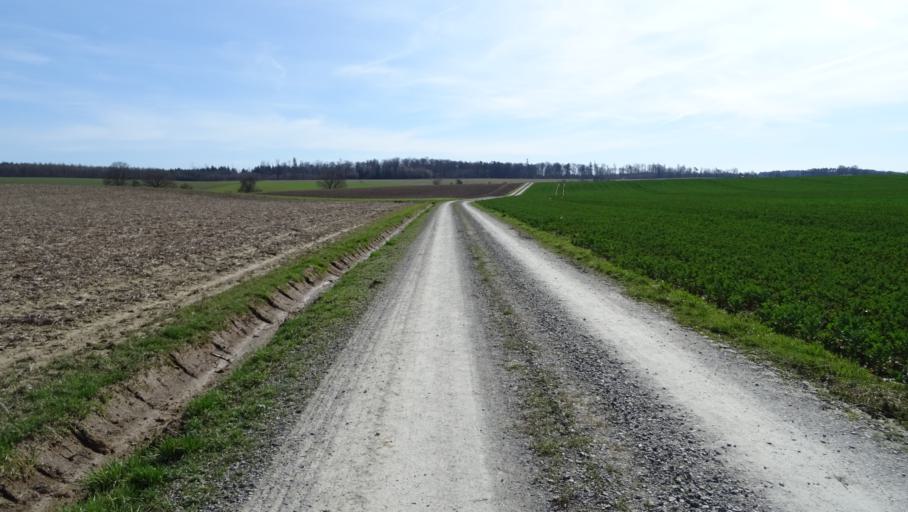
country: DE
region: Baden-Wuerttemberg
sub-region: Karlsruhe Region
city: Seckach
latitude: 49.4100
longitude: 9.3032
